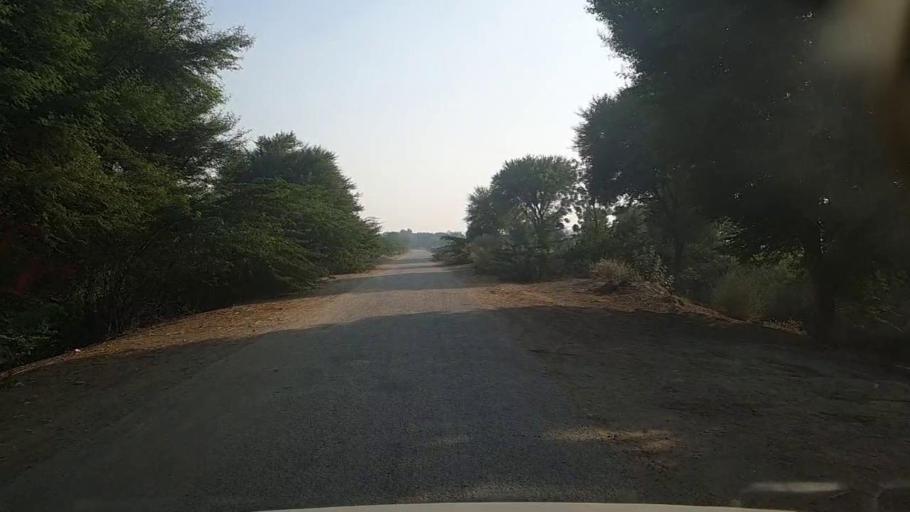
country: PK
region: Sindh
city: Karaundi
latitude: 26.7457
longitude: 68.4769
